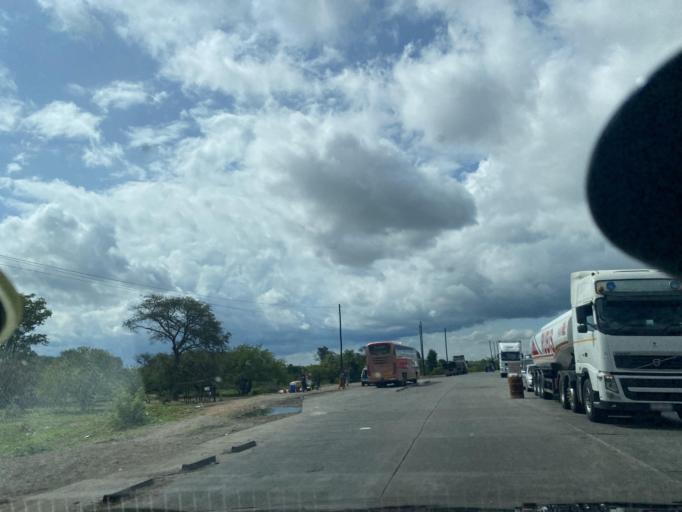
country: ZM
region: Lusaka
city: Kafue
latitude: -15.8432
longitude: 28.2403
